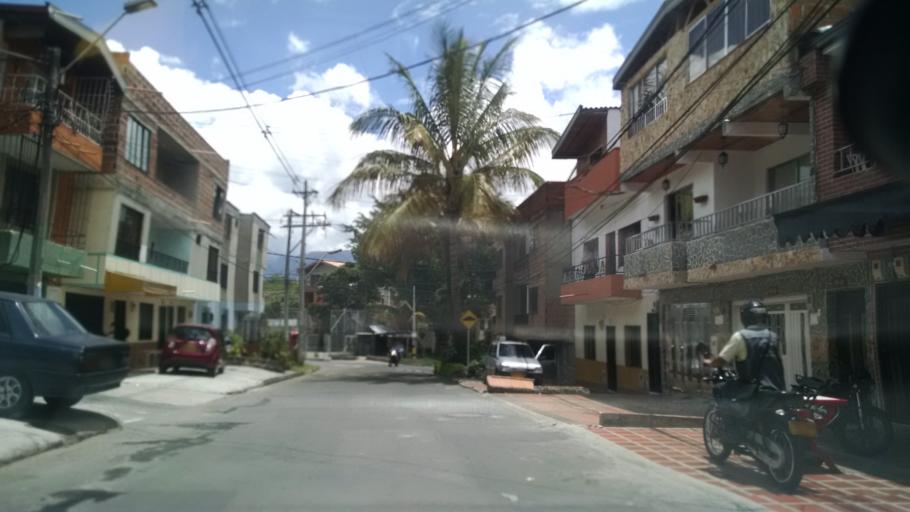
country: CO
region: Antioquia
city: Medellin
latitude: 6.2594
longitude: -75.6093
